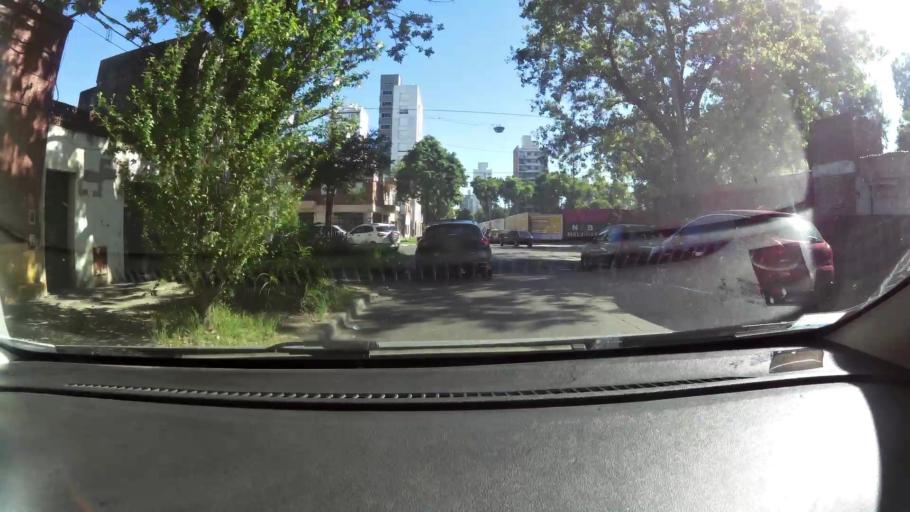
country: AR
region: Santa Fe
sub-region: Departamento de Rosario
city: Rosario
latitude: -32.9501
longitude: -60.6692
